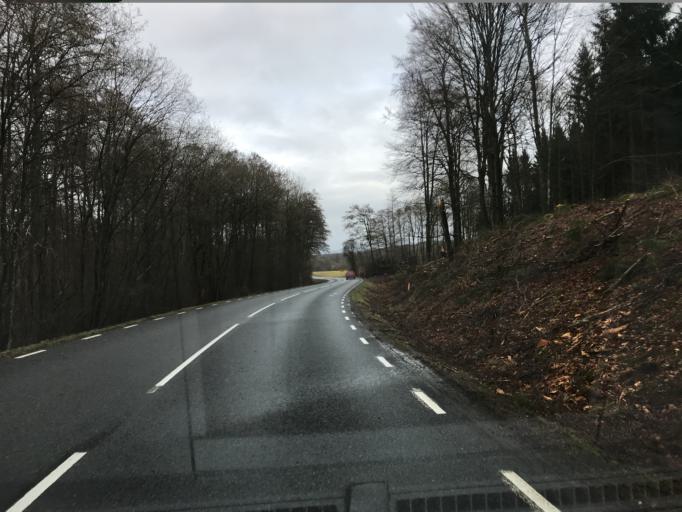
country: SE
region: Skane
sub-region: Hassleholms Kommun
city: Vinslov
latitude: 56.0906
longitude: 13.8362
